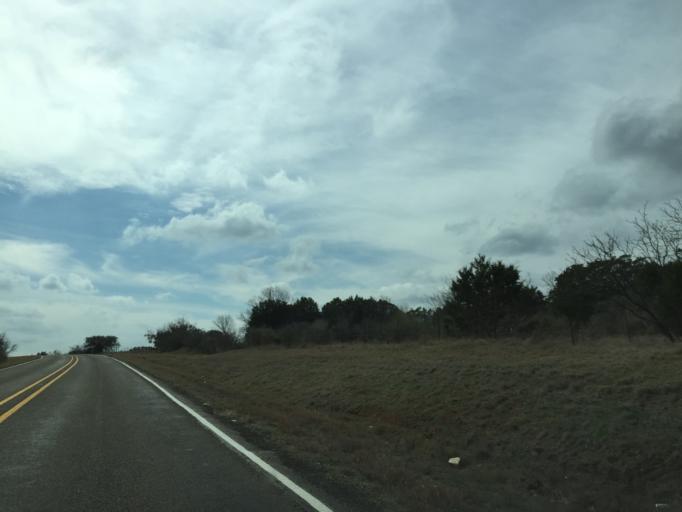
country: US
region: Texas
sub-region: Burnet County
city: Granite Shoals
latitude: 30.5334
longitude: -98.4449
